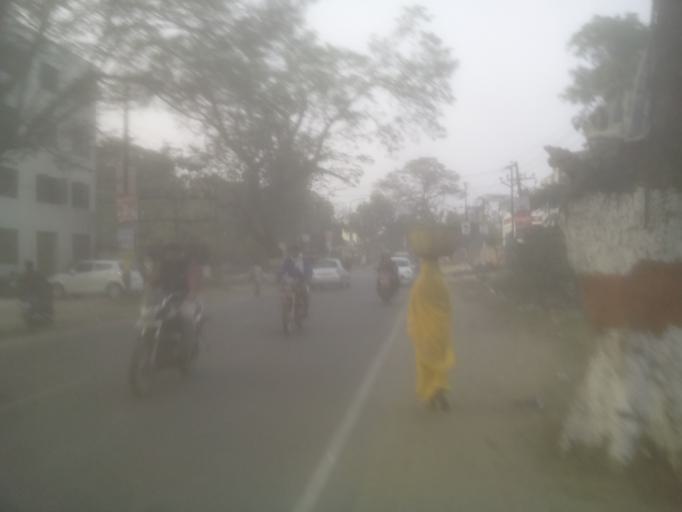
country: IN
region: Jharkhand
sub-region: Dhanbad
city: Dhanbad
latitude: 23.8123
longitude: 86.4326
